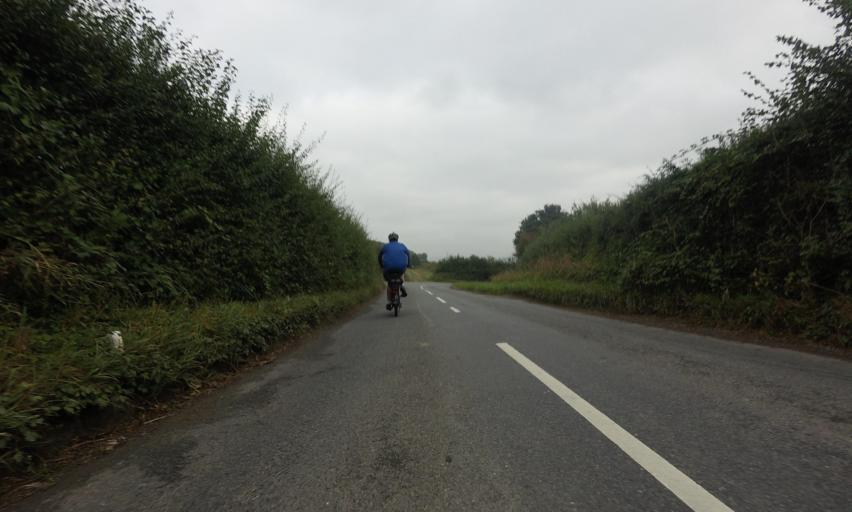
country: GB
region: England
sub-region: Gloucestershire
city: Gotherington
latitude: 51.9684
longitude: -2.0184
